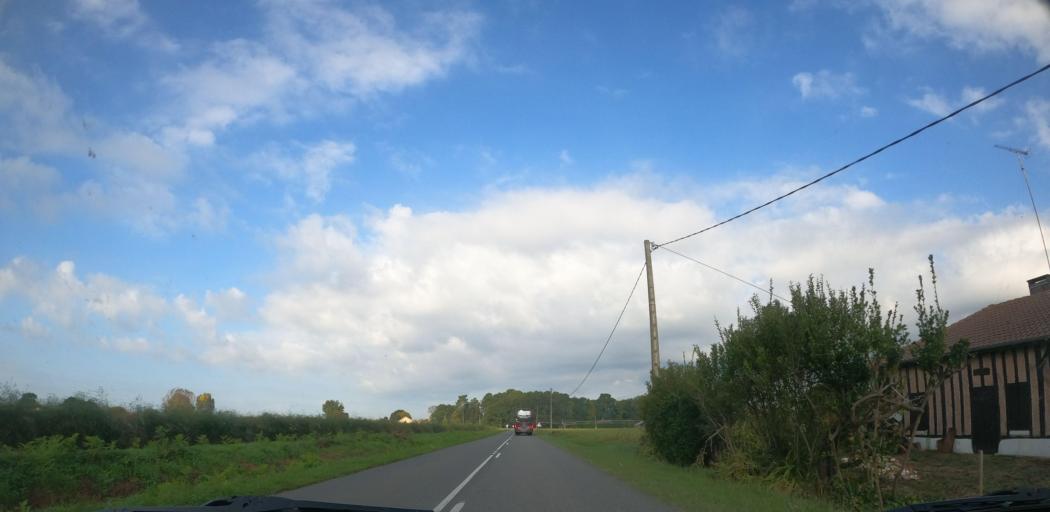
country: FR
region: Aquitaine
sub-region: Departement des Landes
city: Soustons
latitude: 43.7439
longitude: -1.3020
